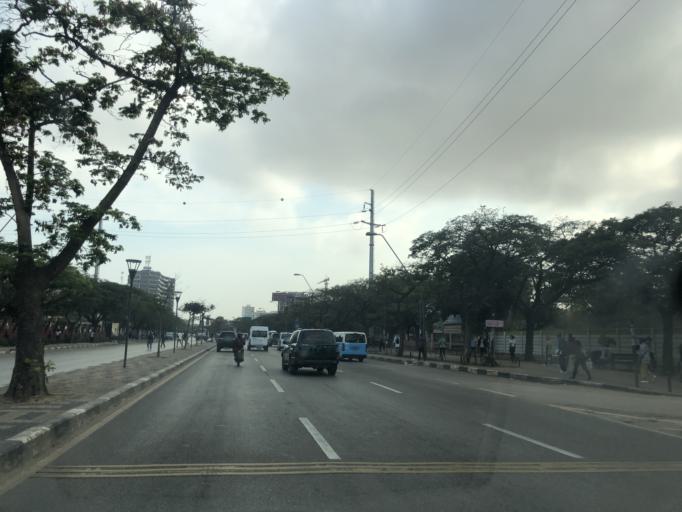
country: AO
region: Luanda
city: Luanda
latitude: -8.8302
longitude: 13.2418
